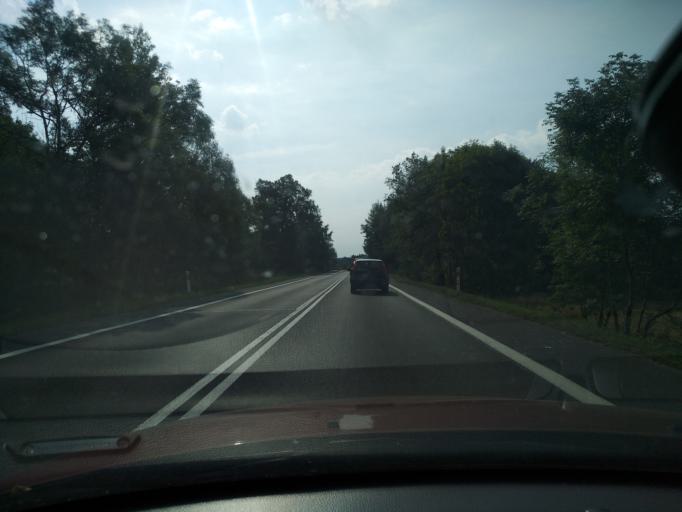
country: PL
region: Lower Silesian Voivodeship
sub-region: Powiat lwowecki
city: Gryfow Slaski
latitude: 51.0177
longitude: 15.4338
